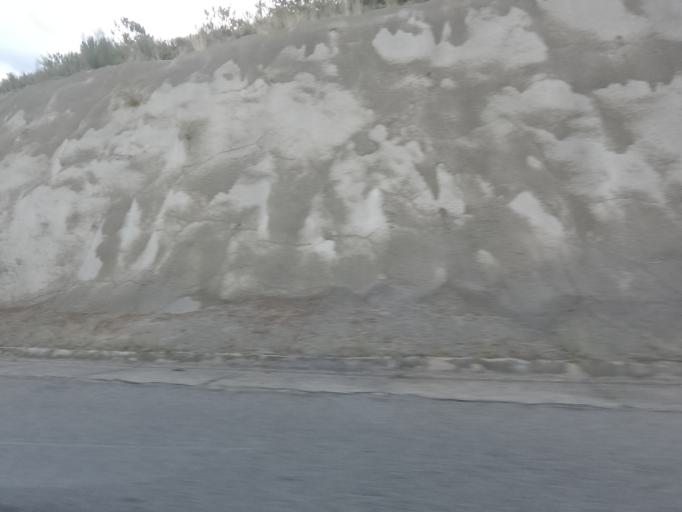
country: PT
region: Viseu
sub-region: Lamego
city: Lamego
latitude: 41.0444
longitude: -7.8600
